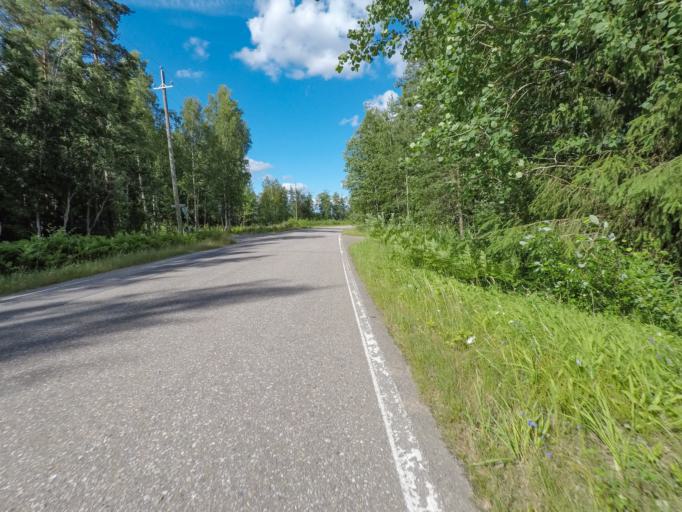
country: FI
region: South Karelia
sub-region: Lappeenranta
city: Joutseno
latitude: 61.1148
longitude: 28.3727
